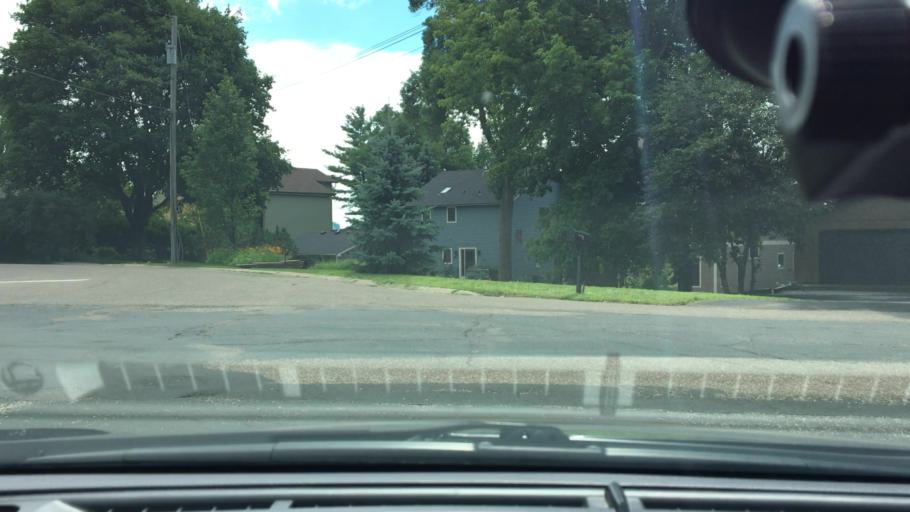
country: US
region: Minnesota
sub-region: Hennepin County
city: New Hope
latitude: 45.0076
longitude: -93.4085
